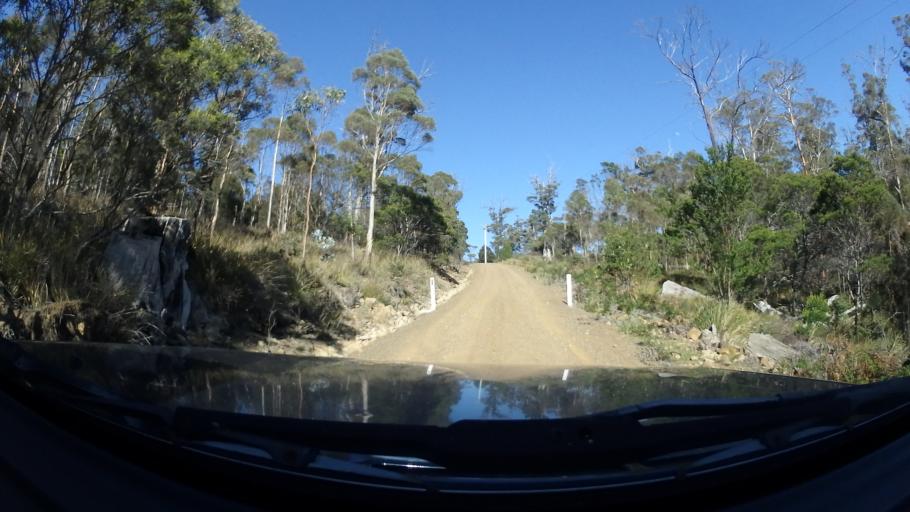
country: AU
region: Tasmania
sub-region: Sorell
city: Sorell
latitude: -42.5419
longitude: 147.8611
